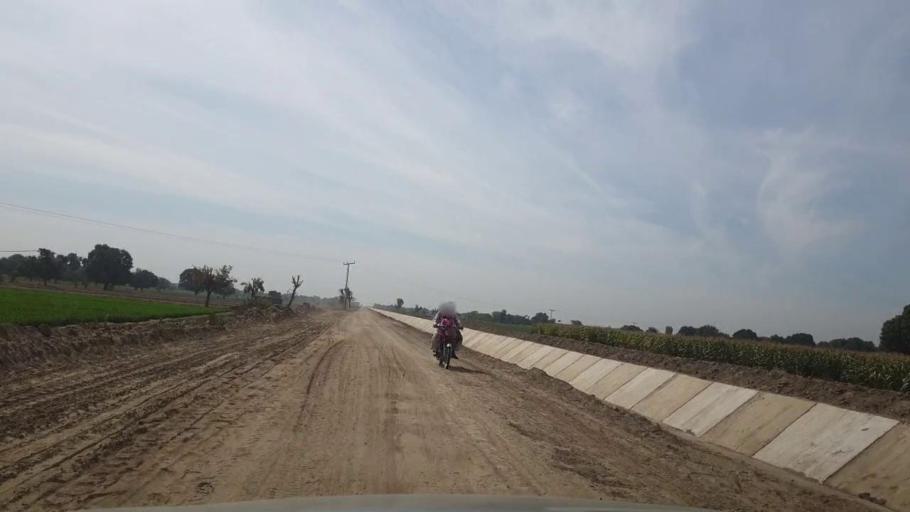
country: PK
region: Sindh
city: Kunri
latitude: 25.1578
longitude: 69.5895
